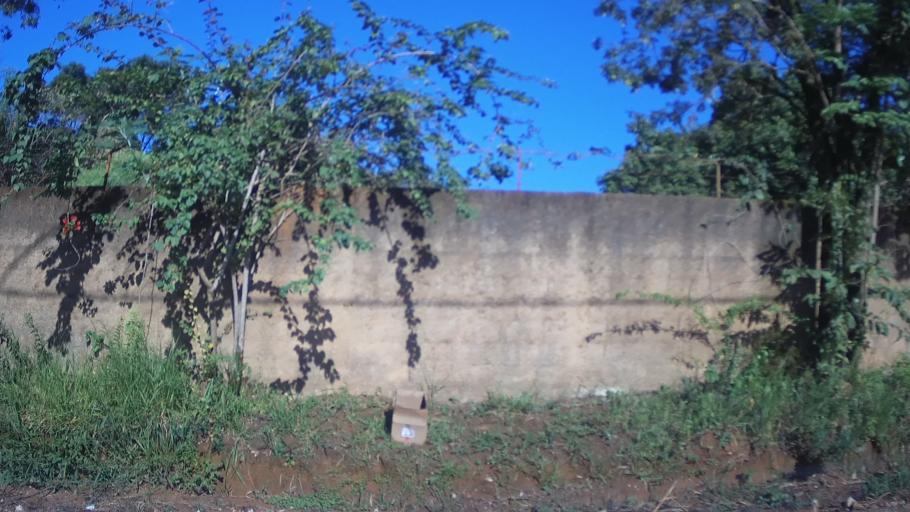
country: BR
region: Sao Paulo
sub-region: Itupeva
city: Itupeva
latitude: -23.1883
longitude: -46.9954
